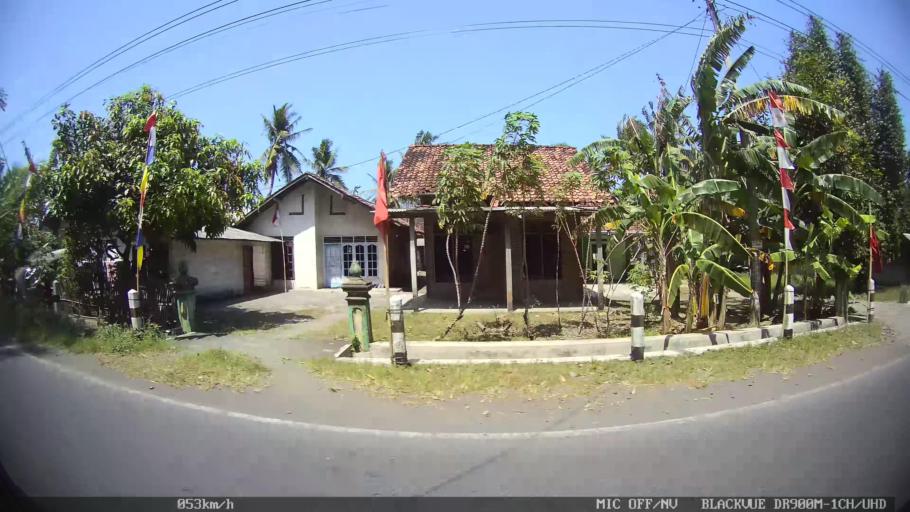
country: ID
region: Daerah Istimewa Yogyakarta
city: Srandakan
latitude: -7.9039
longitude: 110.0752
